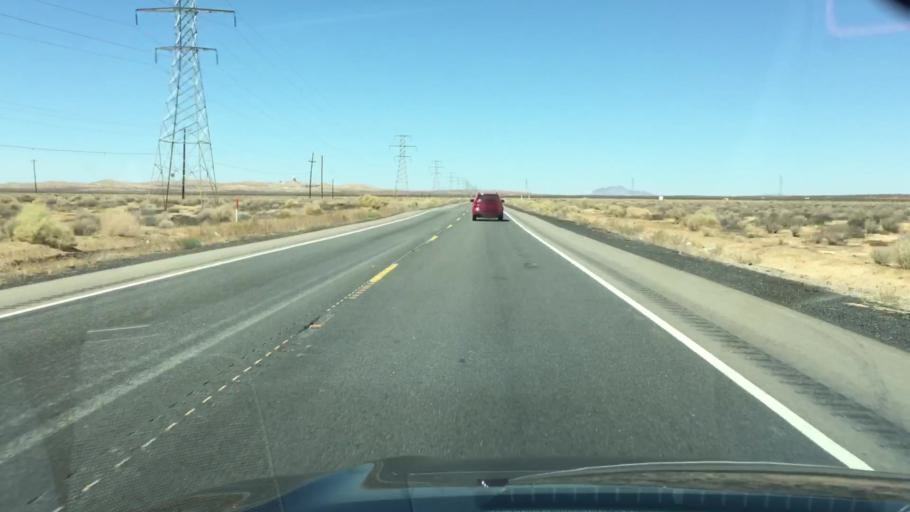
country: US
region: California
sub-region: Kern County
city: Boron
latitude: 35.0251
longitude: -117.5507
